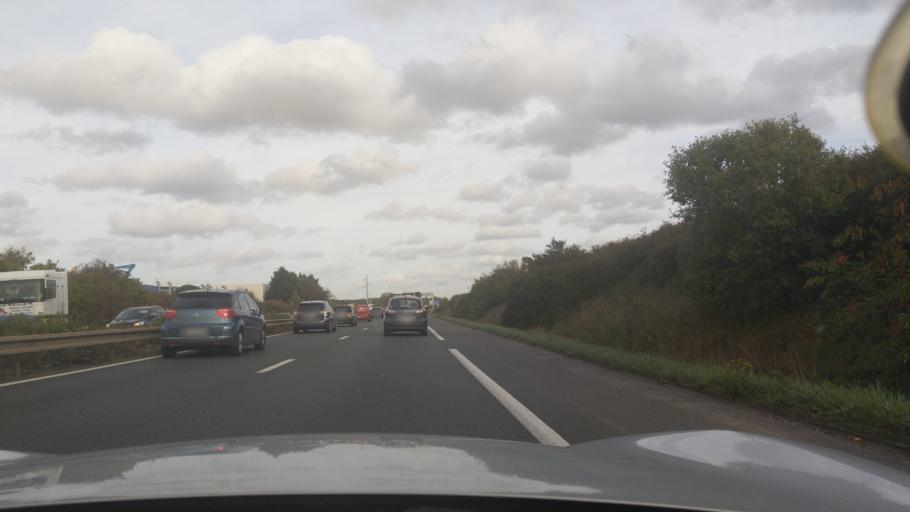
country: FR
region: Ile-de-France
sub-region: Departement du Val-d'Oise
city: Auvers-sur-Oise
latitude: 49.0523
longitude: 2.1586
